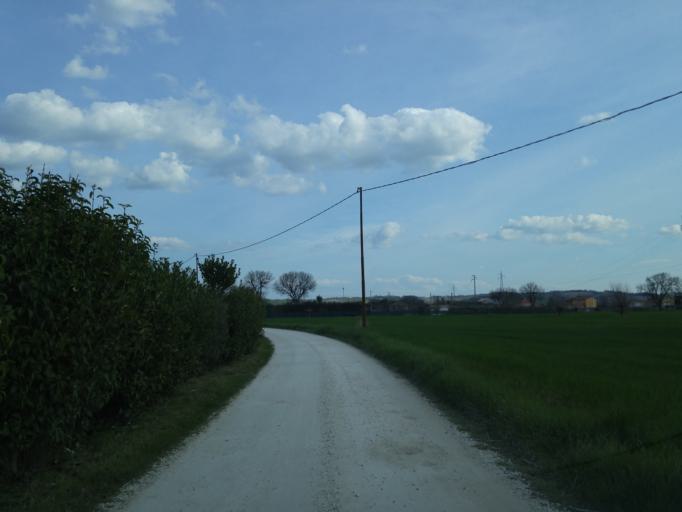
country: IT
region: The Marches
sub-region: Provincia di Pesaro e Urbino
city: Rosciano
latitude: 43.8062
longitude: 12.9987
